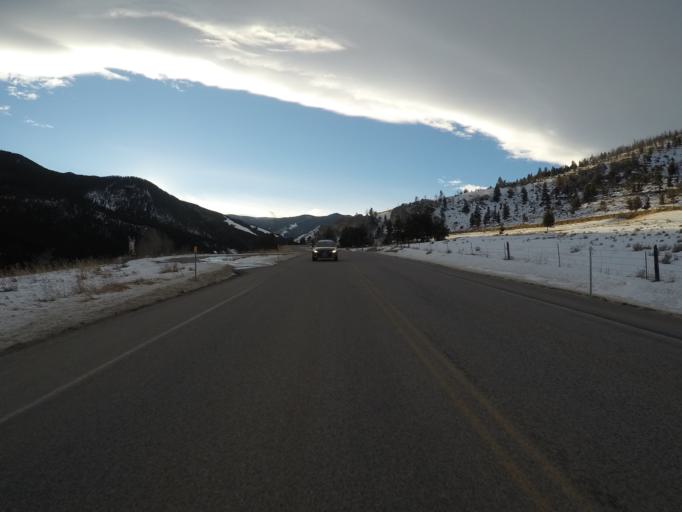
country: US
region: Montana
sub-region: Carbon County
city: Red Lodge
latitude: 45.1574
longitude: -109.3029
